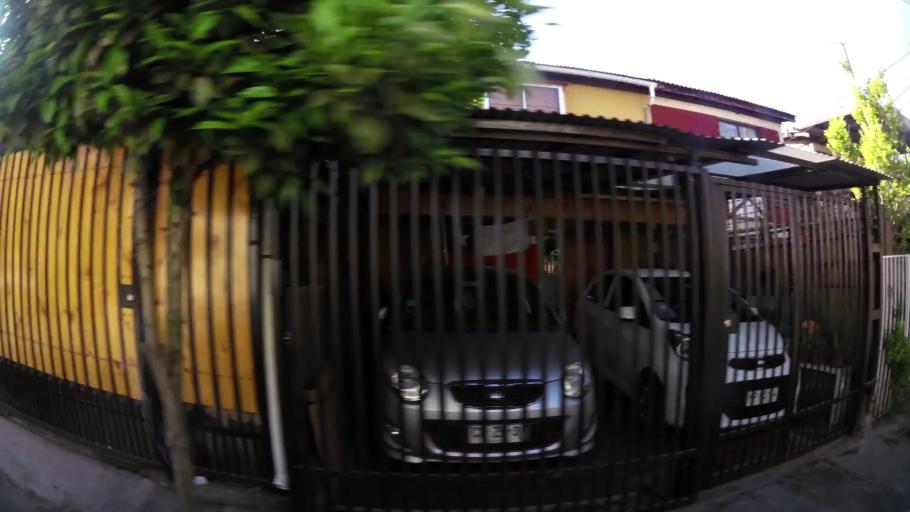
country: CL
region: Santiago Metropolitan
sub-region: Provincia de Santiago
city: Lo Prado
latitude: -33.4811
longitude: -70.7493
